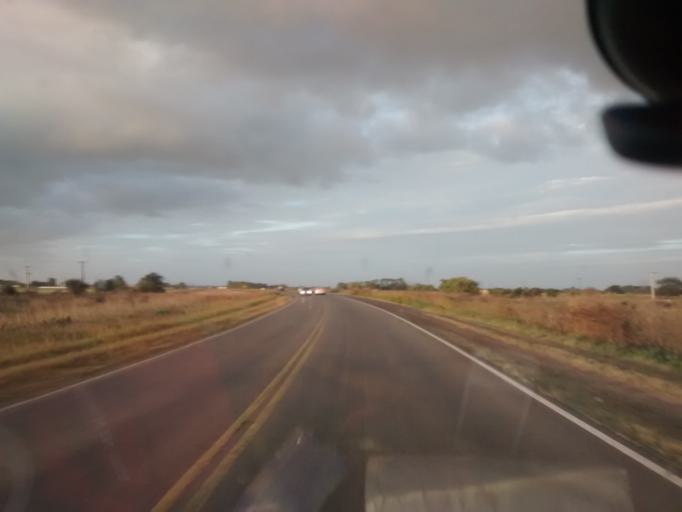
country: AR
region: Buenos Aires
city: Ranchos
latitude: -35.5339
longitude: -58.3700
